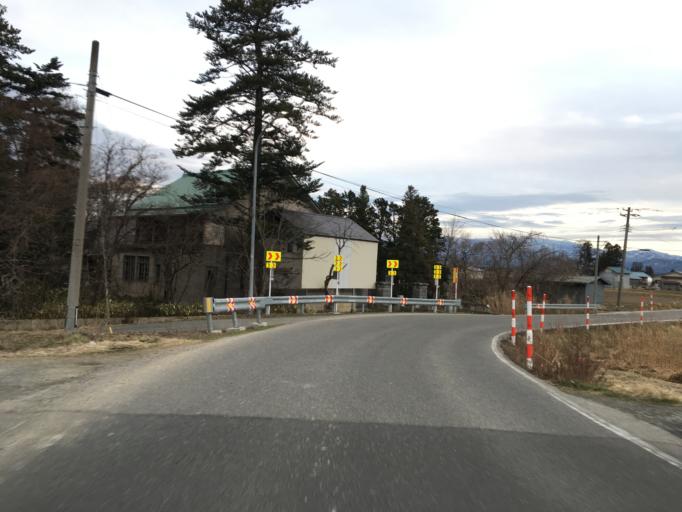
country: JP
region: Yamagata
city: Nagai
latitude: 38.0077
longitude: 140.0762
